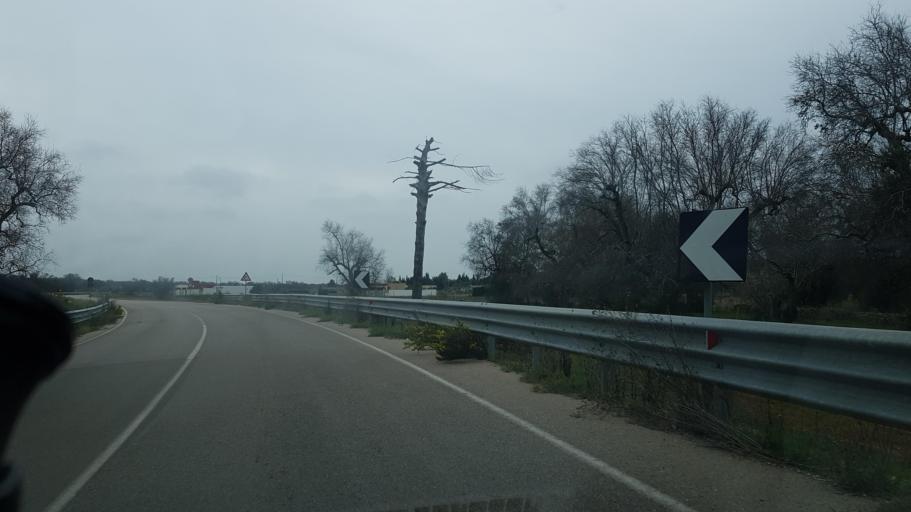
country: IT
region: Apulia
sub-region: Provincia di Brindisi
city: San Pietro Vernotico
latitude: 40.4858
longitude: 18.0109
